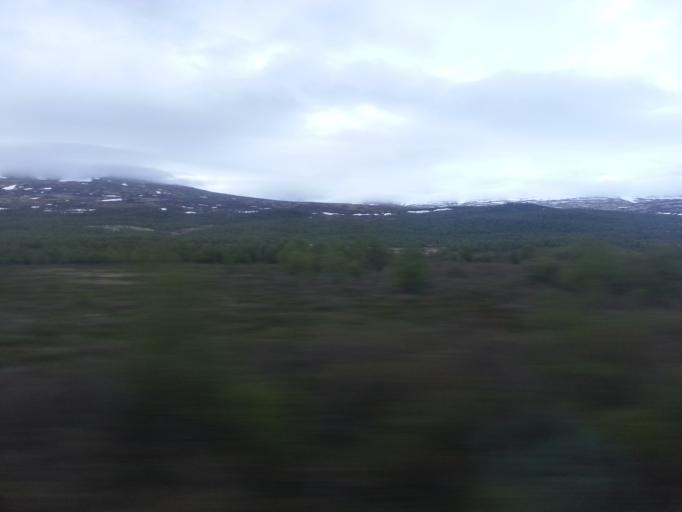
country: NO
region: Oppland
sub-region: Dovre
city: Dovre
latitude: 62.1241
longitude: 9.2836
